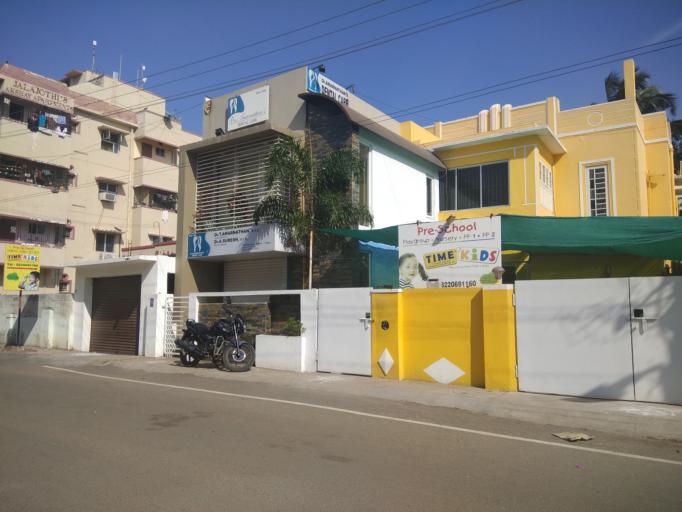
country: IN
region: Tamil Nadu
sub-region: Kancheepuram
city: Pallavaram
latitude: 12.9259
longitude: 80.1271
